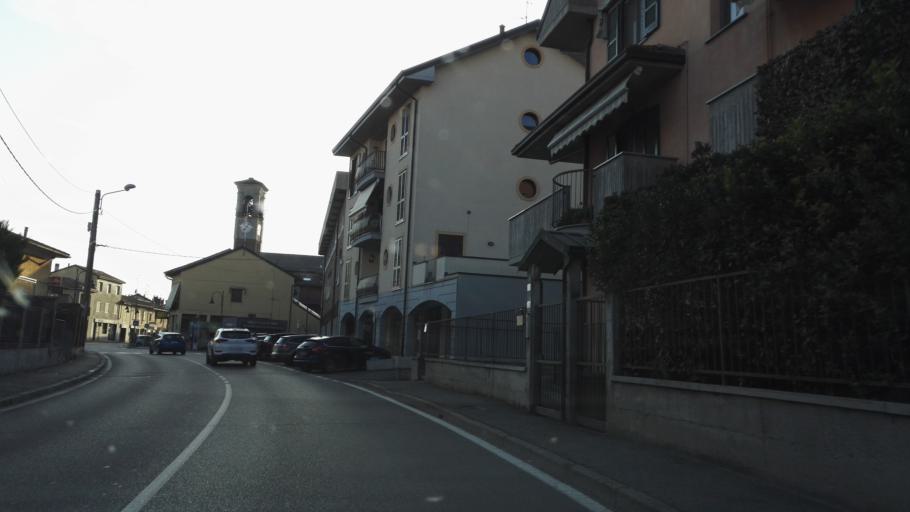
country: IT
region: Lombardy
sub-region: Citta metropolitana di Milano
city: Paullo
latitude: 45.4169
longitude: 9.4035
